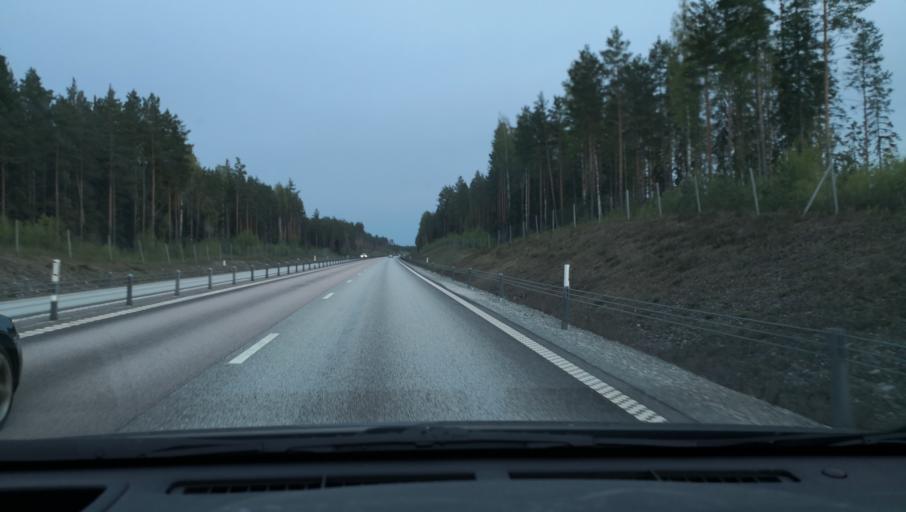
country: SE
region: Vaestmanland
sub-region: Sala Kommun
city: Sala
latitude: 59.9400
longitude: 16.5112
